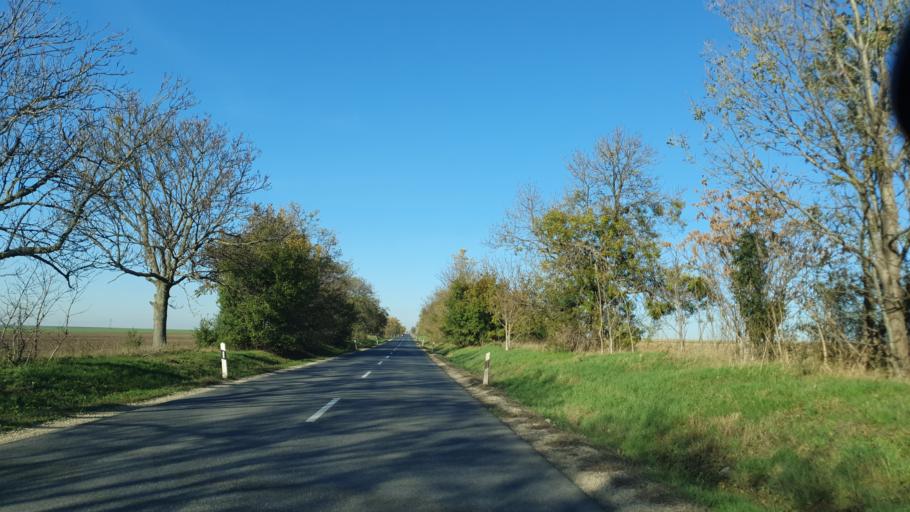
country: HU
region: Fejer
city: Zamoly
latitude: 47.2617
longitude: 18.4193
